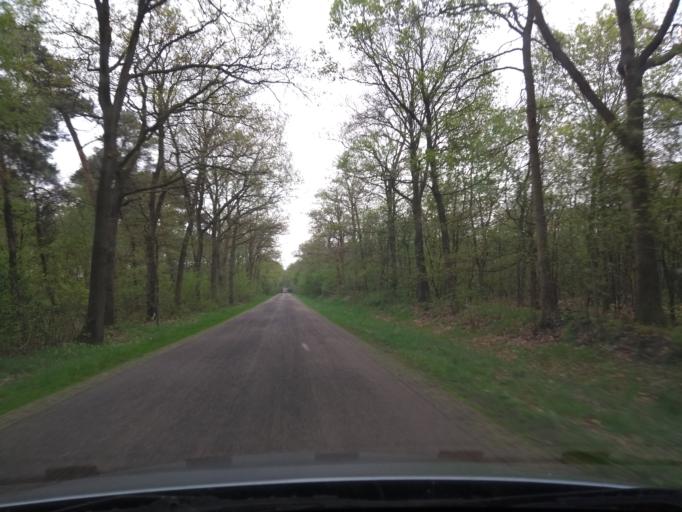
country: DE
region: Lower Saxony
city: Getelo
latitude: 52.4252
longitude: 6.9080
